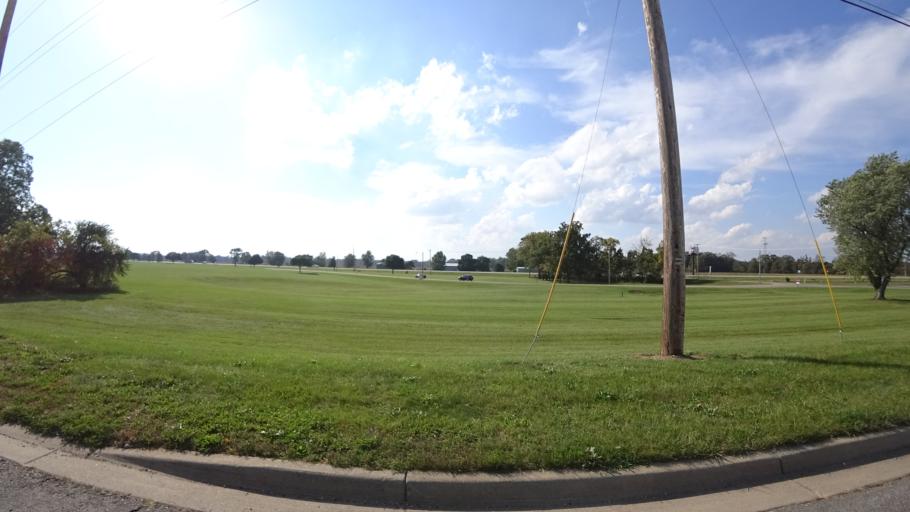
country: US
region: Michigan
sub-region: Saint Joseph County
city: Three Rivers
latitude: 41.9685
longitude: -85.6350
